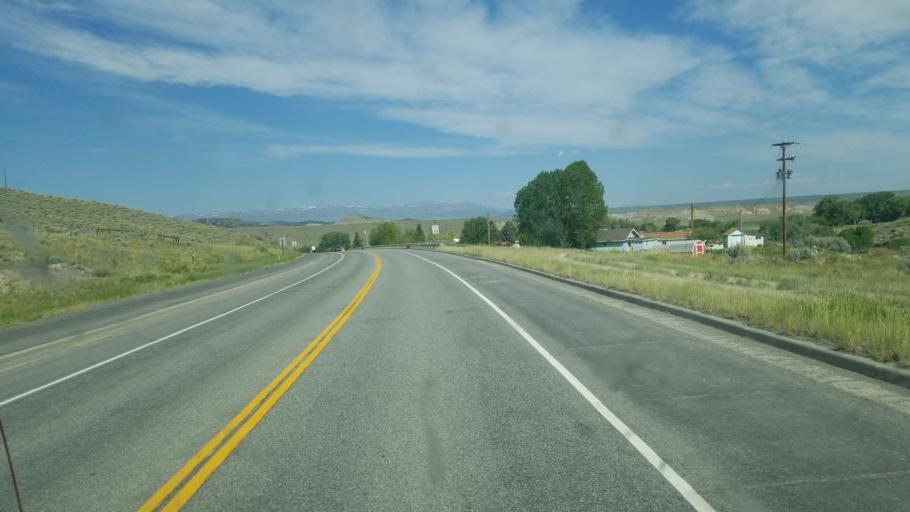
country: US
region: Wyoming
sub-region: Park County
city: Cody
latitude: 44.1549
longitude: -108.8648
